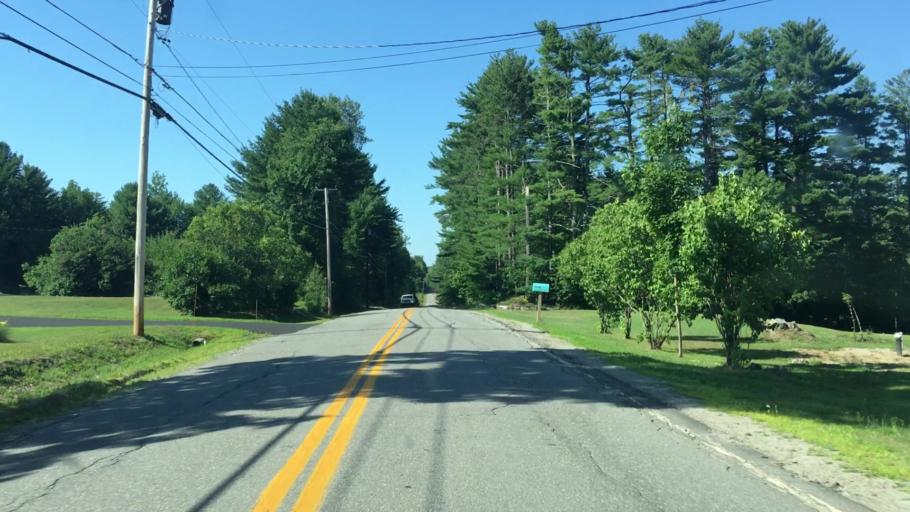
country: US
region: Maine
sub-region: Penobscot County
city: Enfield
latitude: 45.2576
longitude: -68.5637
